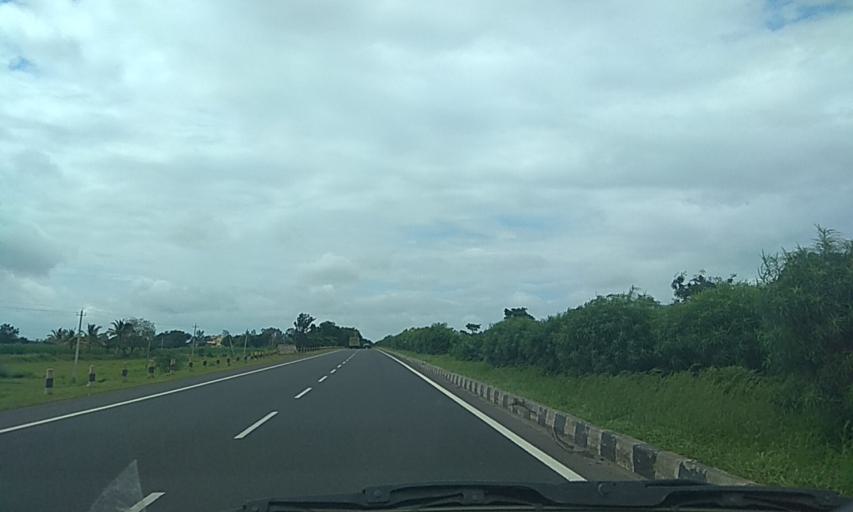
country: IN
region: Maharashtra
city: Nipani
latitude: 16.3689
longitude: 74.4019
